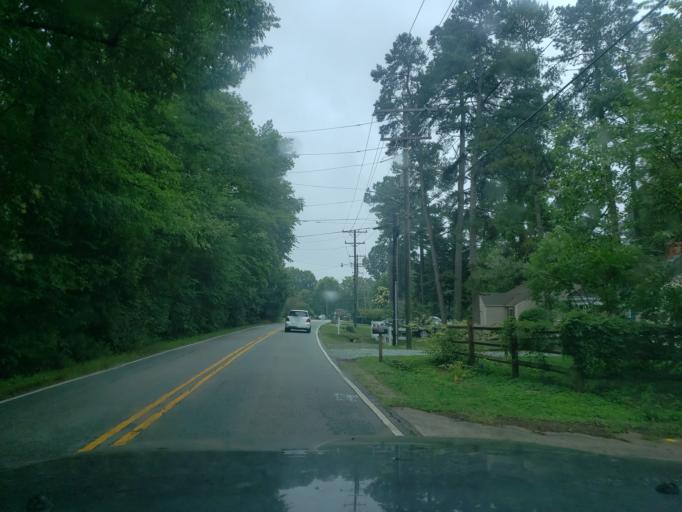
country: US
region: North Carolina
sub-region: Durham County
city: Durham
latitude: 35.9741
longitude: -78.9165
